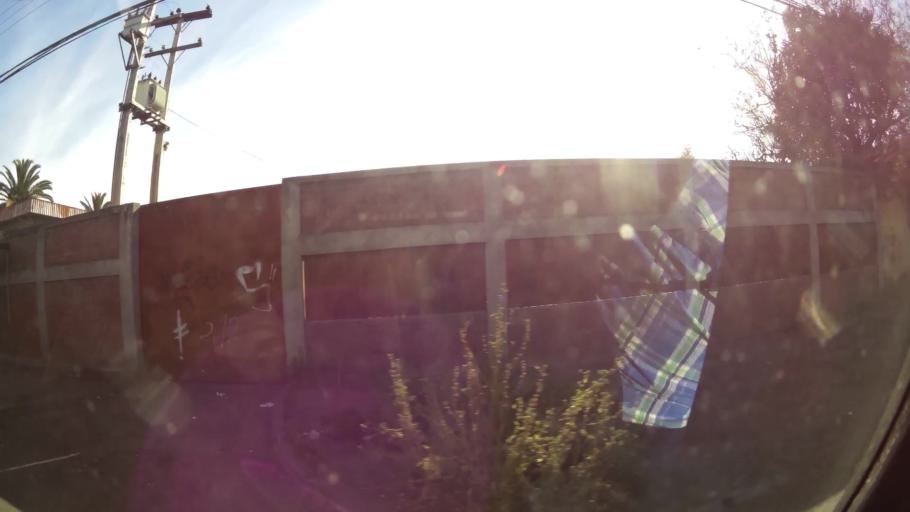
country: CL
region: Santiago Metropolitan
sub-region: Provincia de Santiago
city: Santiago
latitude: -33.4657
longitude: -70.6829
